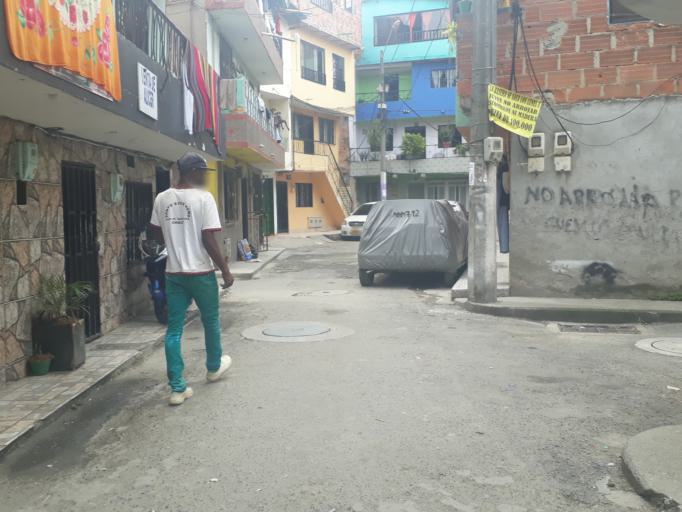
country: CO
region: Antioquia
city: Medellin
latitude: 6.2773
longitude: -75.5662
